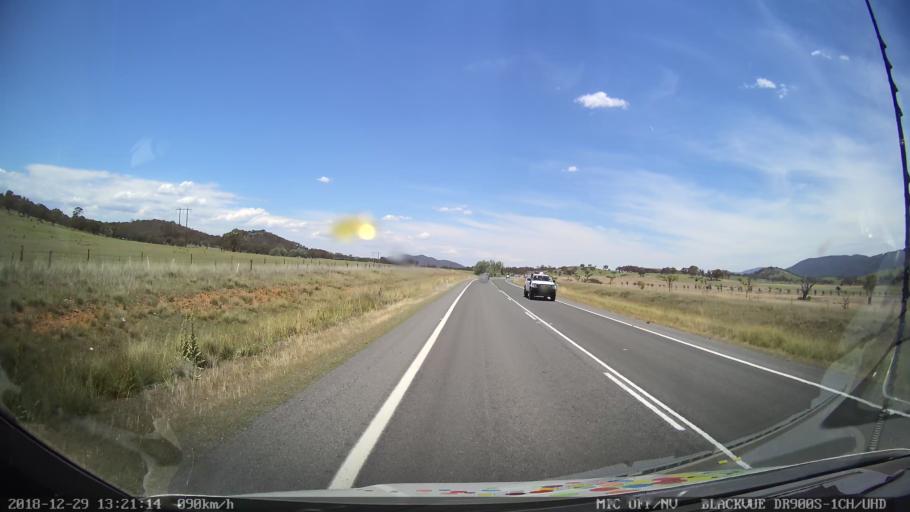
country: AU
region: Australian Capital Territory
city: Macarthur
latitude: -35.7896
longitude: 149.1636
